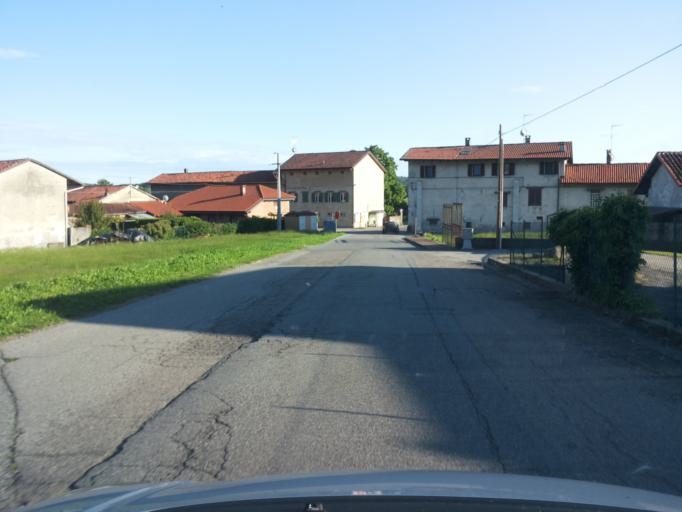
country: IT
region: Piedmont
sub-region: Provincia di Torino
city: Piverone
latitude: 45.4418
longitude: 8.0118
